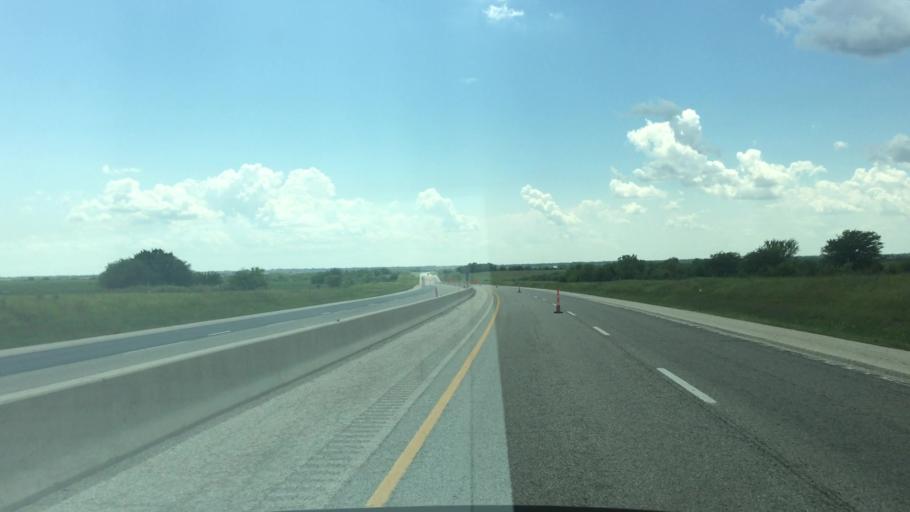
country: US
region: Kansas
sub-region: Shawnee County
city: Auburn
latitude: 38.7930
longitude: -95.9106
